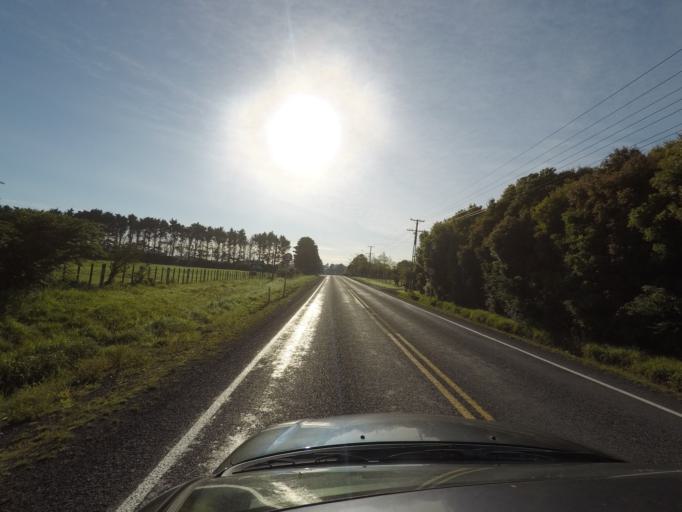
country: NZ
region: Auckland
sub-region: Auckland
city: Takanini
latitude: -37.0182
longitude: 174.9328
